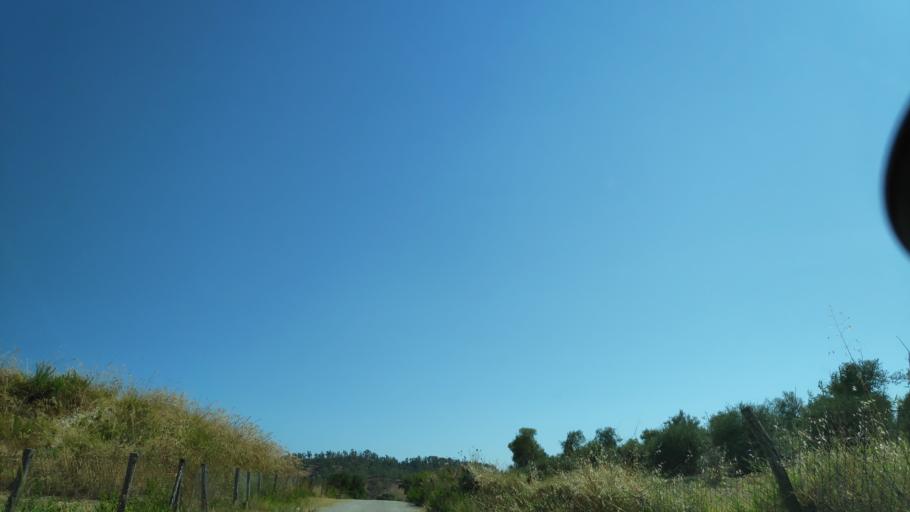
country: IT
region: Calabria
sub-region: Provincia di Reggio Calabria
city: Monasterace
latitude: 38.4324
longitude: 16.5249
